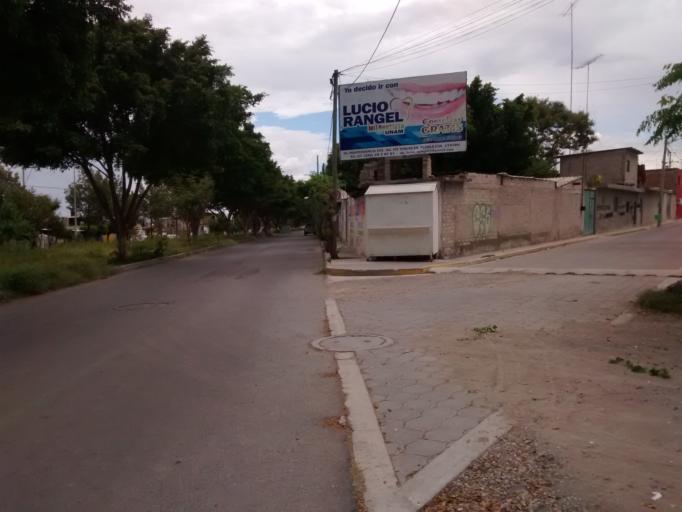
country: MX
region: Puebla
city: Tehuacan
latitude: 18.4700
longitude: -97.4050
